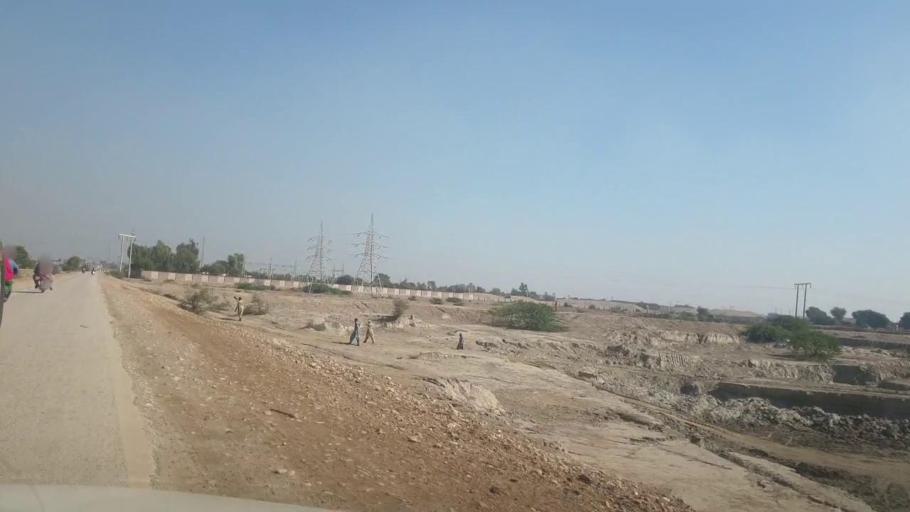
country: PK
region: Sindh
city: Bhan
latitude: 26.5468
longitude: 67.7096
